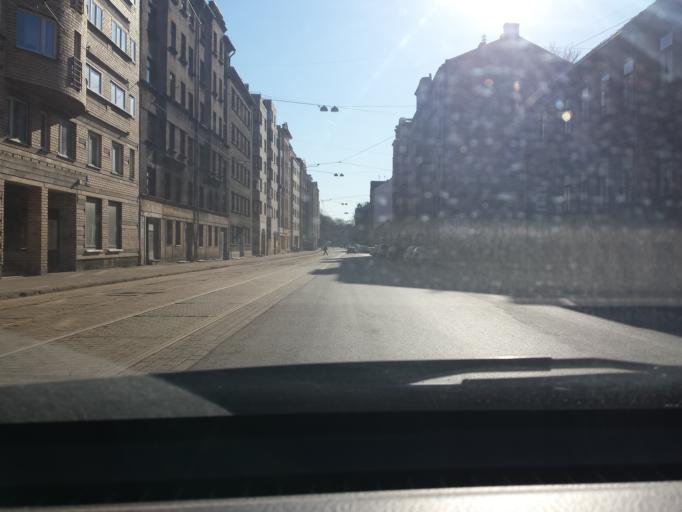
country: LV
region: Riga
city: Riga
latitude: 56.9760
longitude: 24.1446
